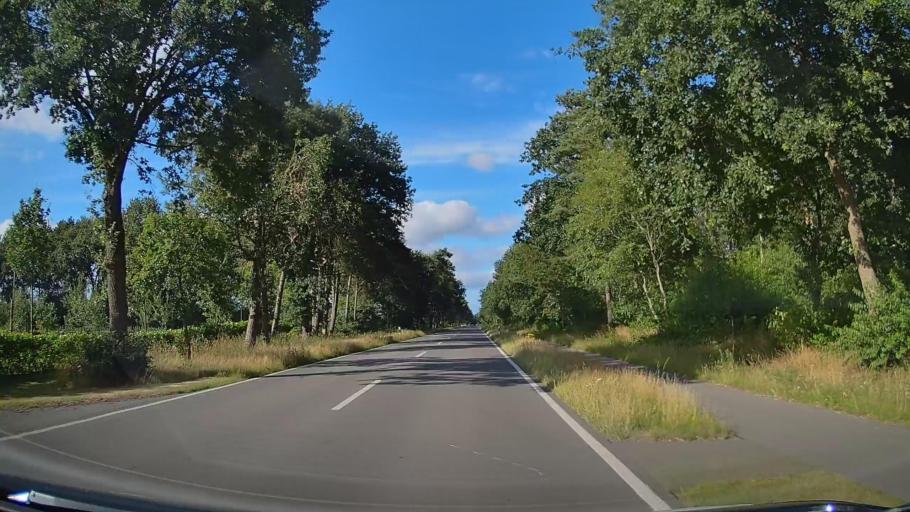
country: DE
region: Lower Saxony
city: Bosel
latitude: 52.9498
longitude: 7.8983
